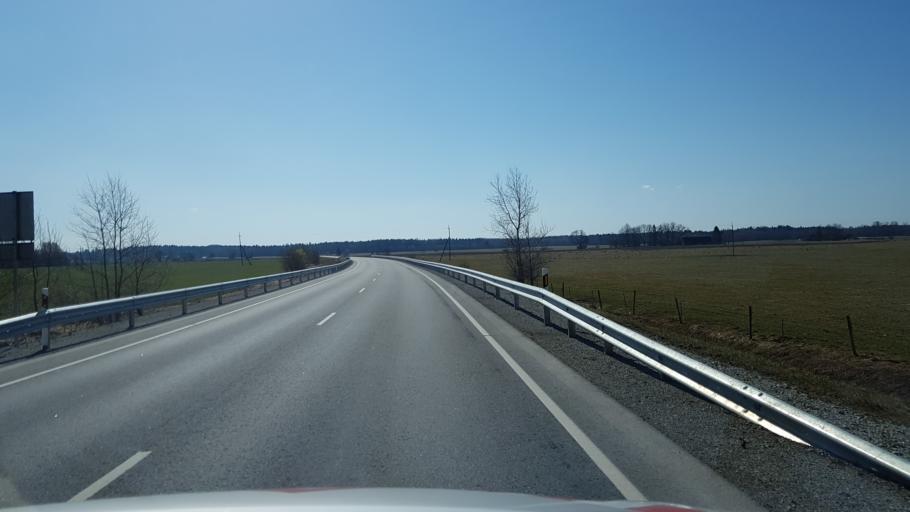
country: EE
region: Ida-Virumaa
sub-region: Kohtla-Jaerve linn
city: Kohtla-Jarve
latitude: 59.3485
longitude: 27.2428
